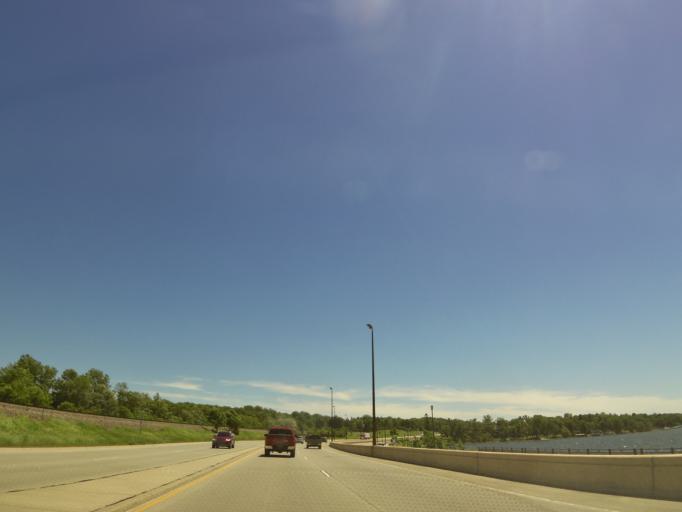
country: US
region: Minnesota
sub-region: Becker County
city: Detroit Lakes
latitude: 46.8048
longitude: -95.8136
